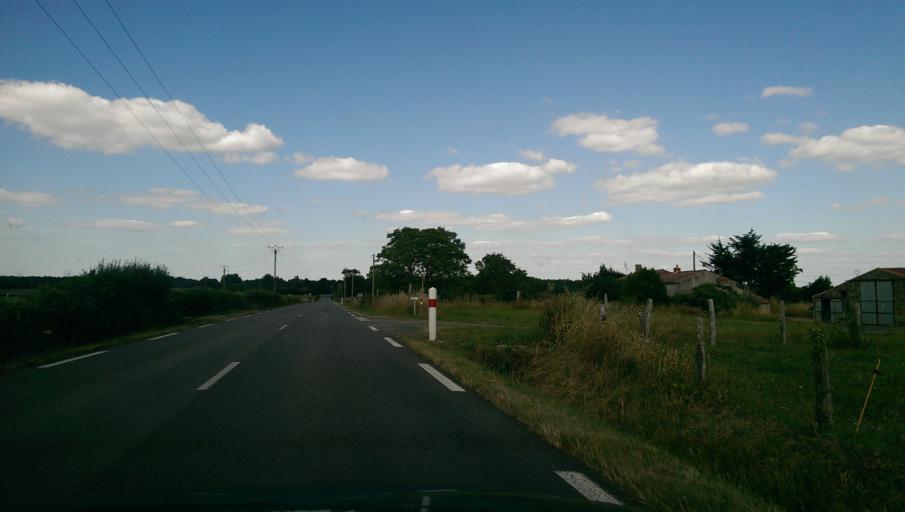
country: FR
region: Pays de la Loire
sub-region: Departement de la Vendee
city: Rocheserviere
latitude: 46.9161
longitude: -1.5448
